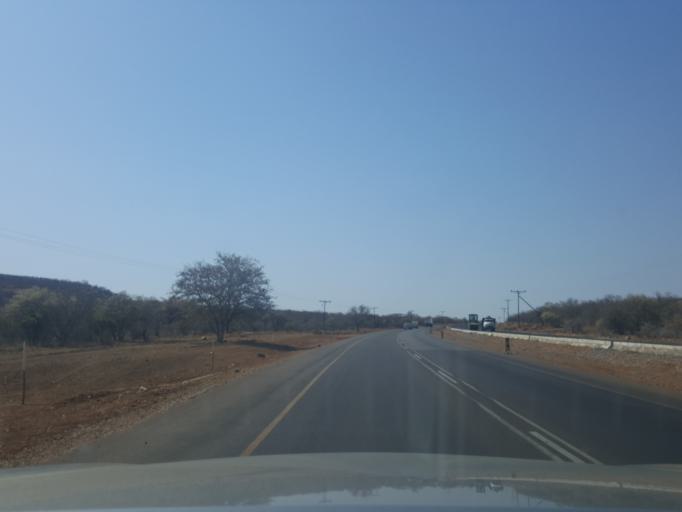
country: BW
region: Kweneng
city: Gabane
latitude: -24.7536
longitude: 25.8285
